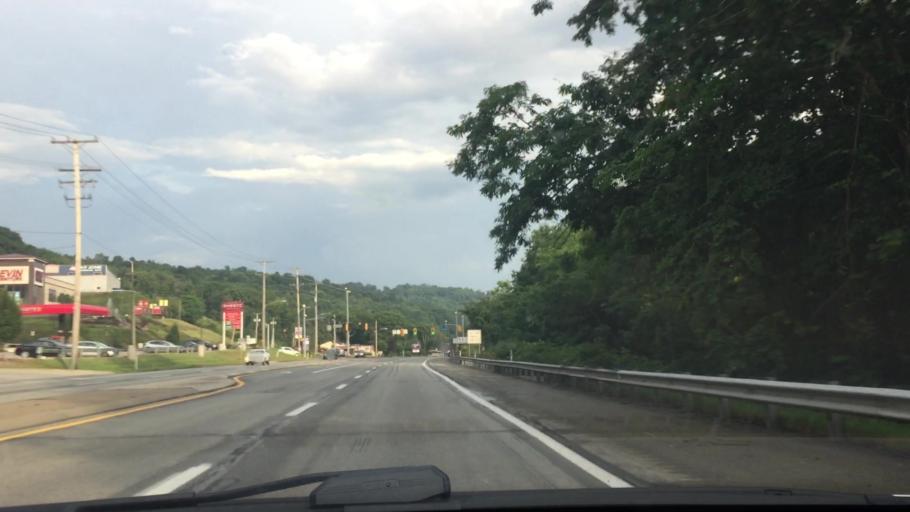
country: US
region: Pennsylvania
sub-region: Westmoreland County
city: Murrysville
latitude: 40.4352
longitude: -79.7341
